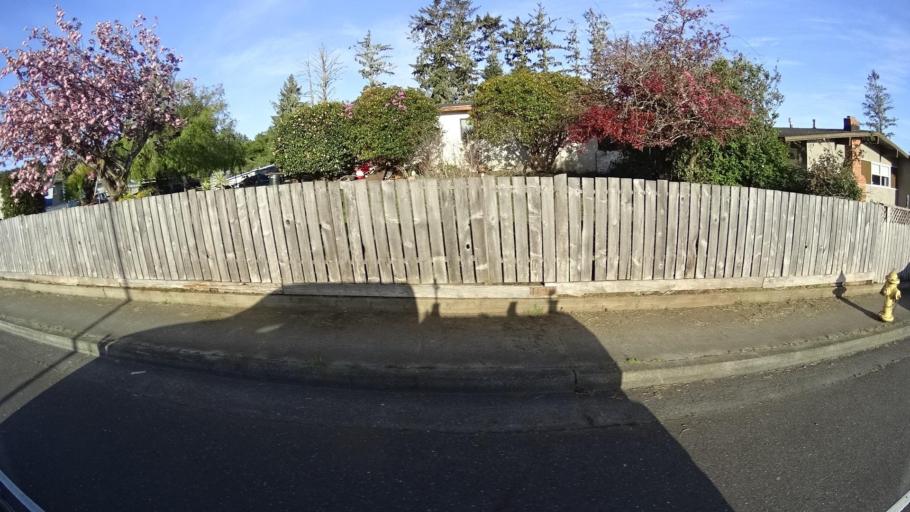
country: US
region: California
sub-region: Humboldt County
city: Humboldt Hill
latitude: 40.7337
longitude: -124.2021
